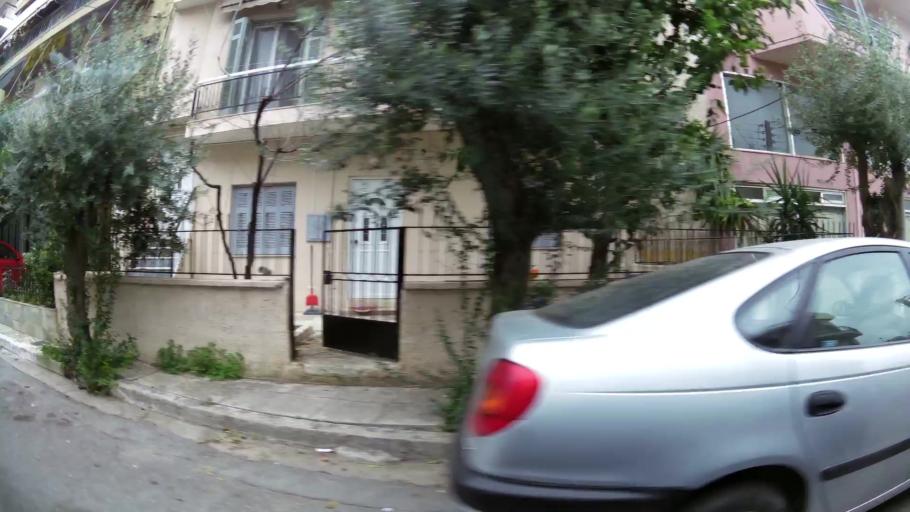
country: GR
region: Attica
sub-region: Nomarchia Athinas
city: Chaidari
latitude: 38.0026
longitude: 23.6722
